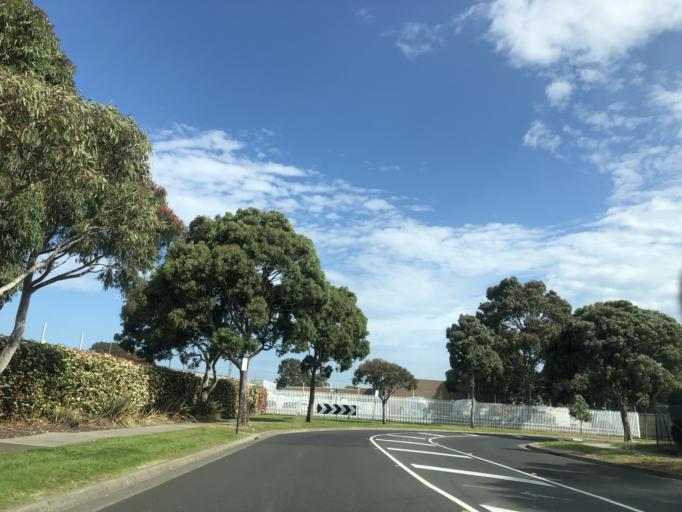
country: AU
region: Victoria
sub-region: Monash
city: Notting Hill
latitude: -37.9213
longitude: 145.1548
